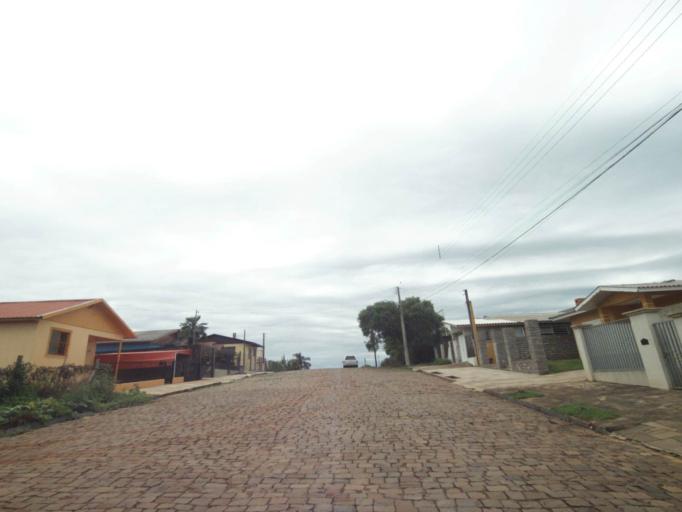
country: BR
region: Rio Grande do Sul
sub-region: Lagoa Vermelha
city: Lagoa Vermelha
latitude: -28.2129
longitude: -51.5313
